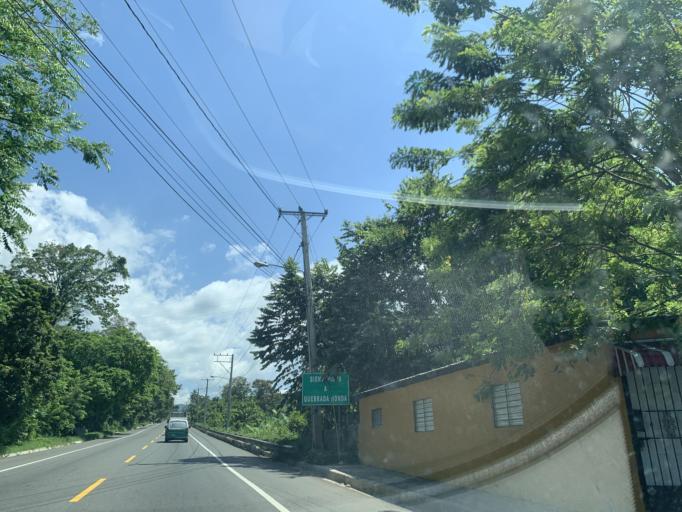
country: DO
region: Puerto Plata
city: Altamira
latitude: 19.7093
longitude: -70.8365
